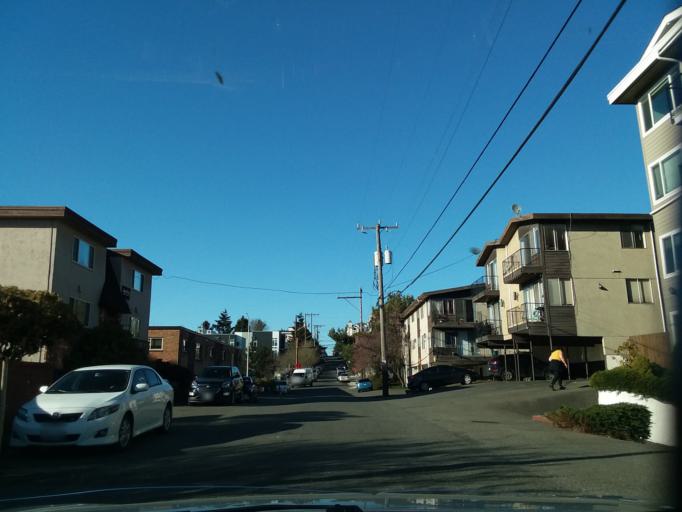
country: US
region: Washington
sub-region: King County
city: Shoreline
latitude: 47.6917
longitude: -122.3539
